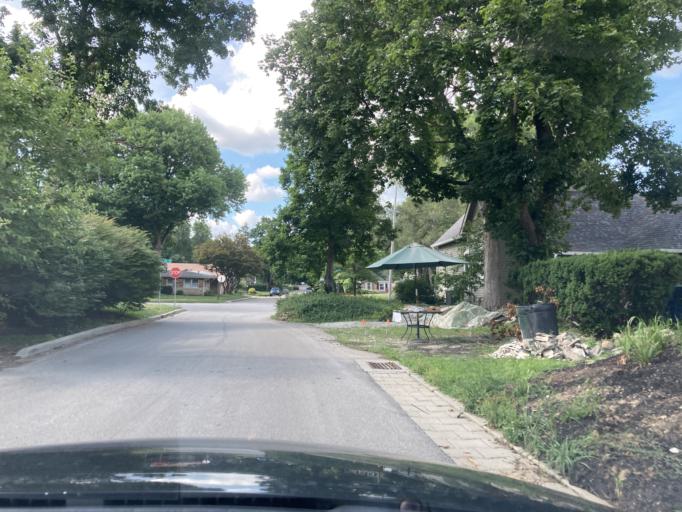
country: US
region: Indiana
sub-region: Marion County
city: Broad Ripple
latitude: 39.8618
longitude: -86.1340
